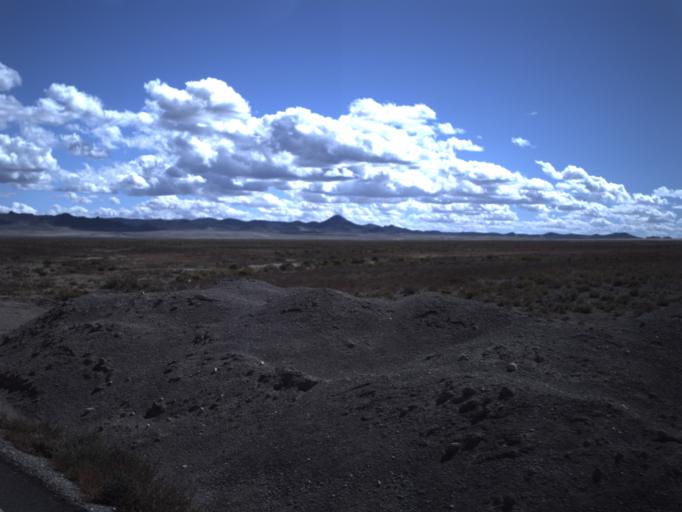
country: US
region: Utah
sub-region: Beaver County
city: Milford
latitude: 38.4768
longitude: -113.4263
